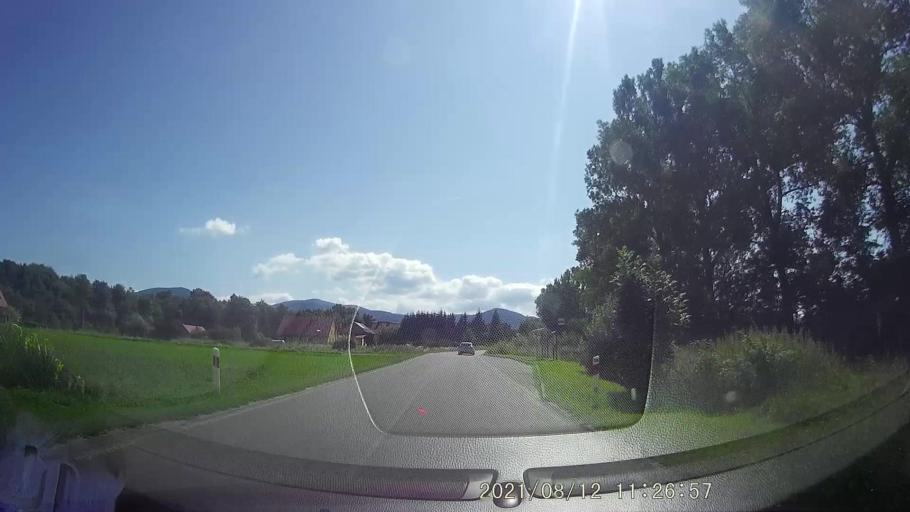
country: PL
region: Lower Silesian Voivodeship
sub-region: Powiat klodzki
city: Bystrzyca Klodzka
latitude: 50.2730
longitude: 16.6902
